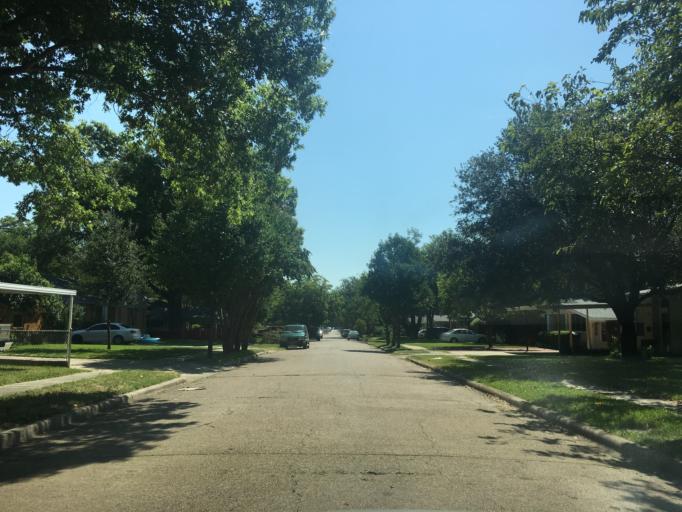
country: US
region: Texas
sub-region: Dallas County
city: Garland
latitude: 32.8525
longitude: -96.6701
